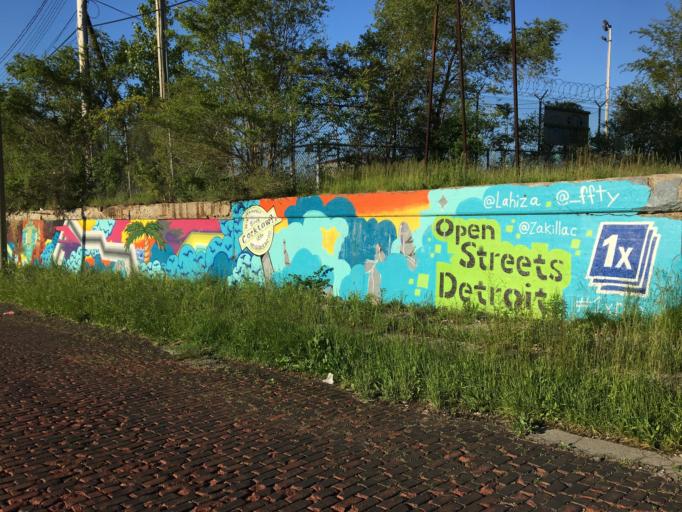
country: US
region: Michigan
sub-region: Wayne County
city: Detroit
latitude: 42.3295
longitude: -83.0792
